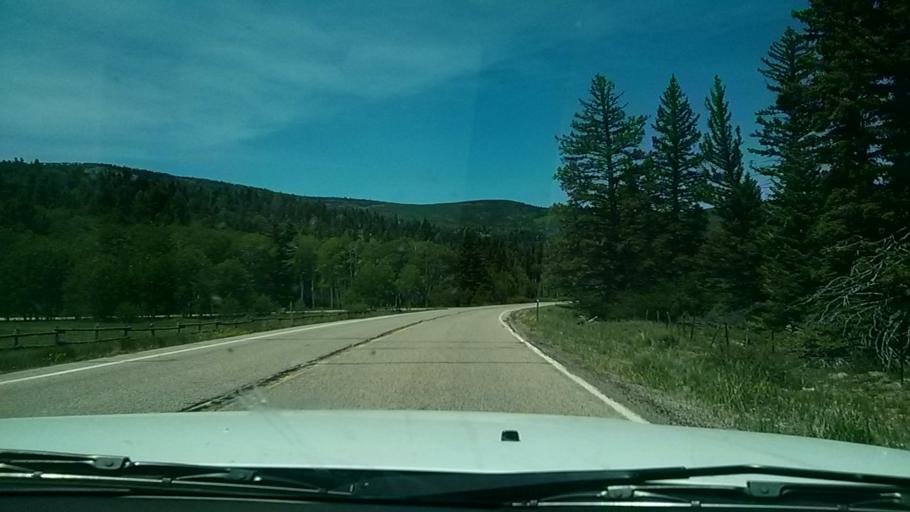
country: US
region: Utah
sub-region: Iron County
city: Cedar City
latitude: 37.5945
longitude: -112.9154
